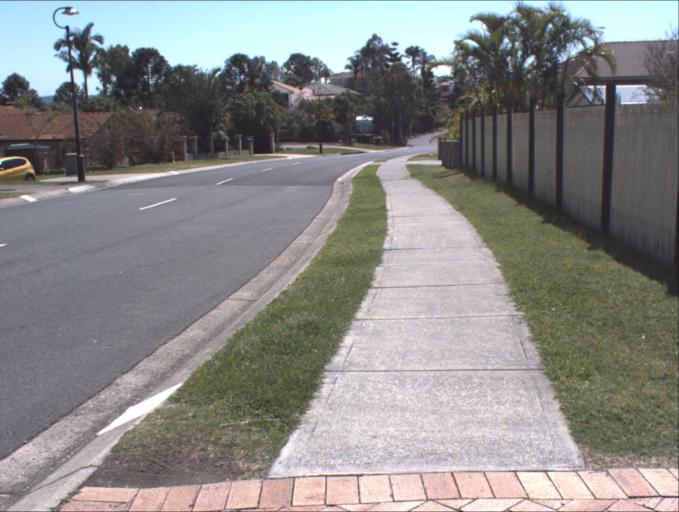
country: AU
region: Queensland
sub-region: Logan
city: Waterford West
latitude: -27.7072
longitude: 153.1630
